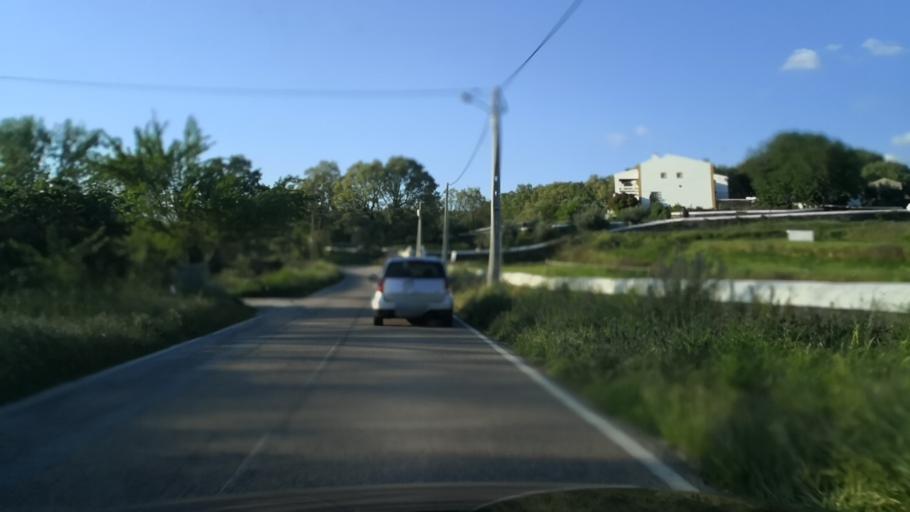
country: PT
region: Portalegre
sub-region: Marvao
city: Marvao
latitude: 39.3503
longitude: -7.4056
